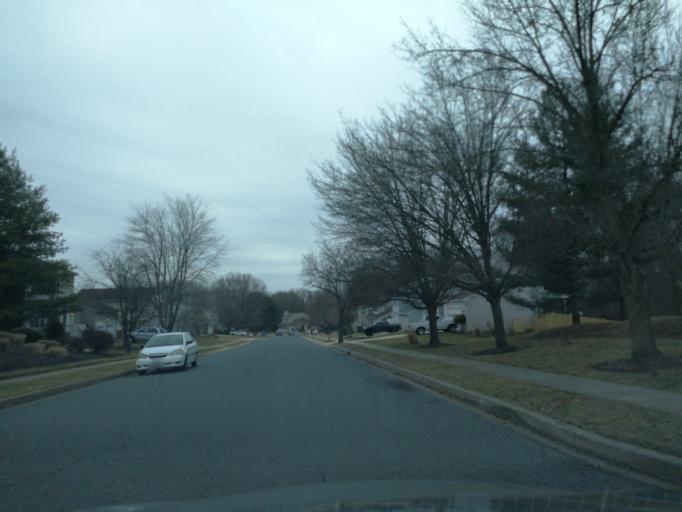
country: US
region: Maryland
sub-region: Harford County
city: Joppatowne
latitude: 39.4664
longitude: -76.3253
